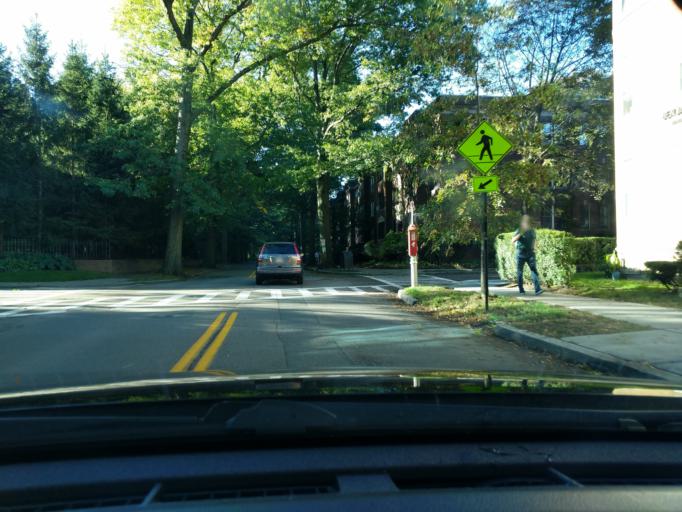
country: US
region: Massachusetts
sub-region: Norfolk County
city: Brookline
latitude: 42.3494
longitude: -71.1141
